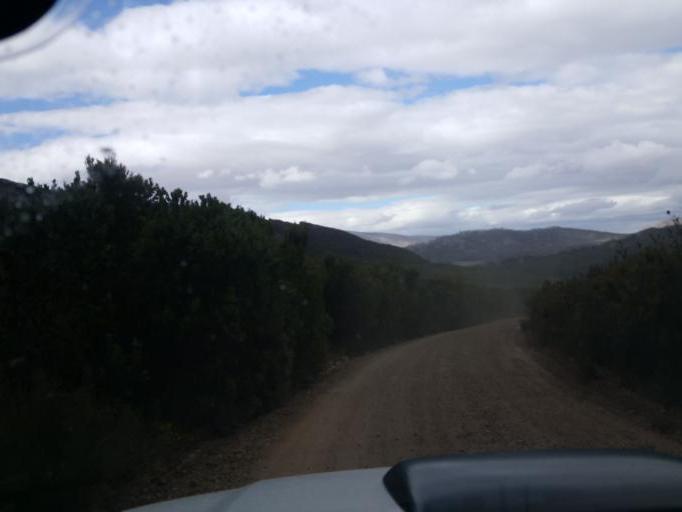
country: ZA
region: Western Cape
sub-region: Eden District Municipality
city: George
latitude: -33.8815
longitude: 22.4366
